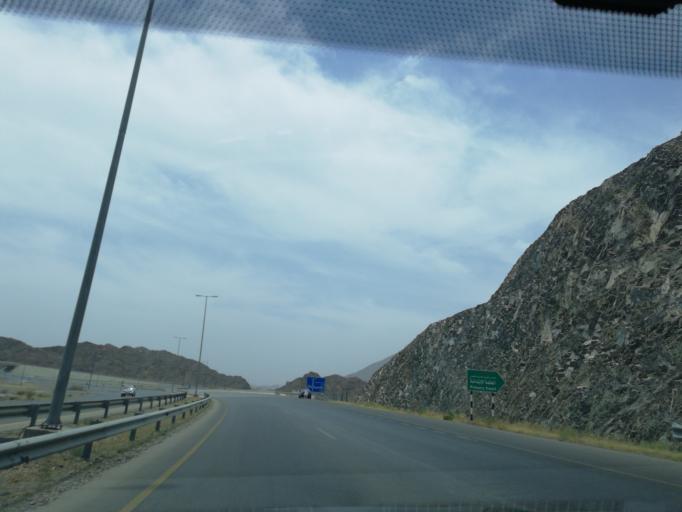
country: OM
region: Muhafazat ad Dakhiliyah
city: Izki
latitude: 22.9761
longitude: 57.7812
